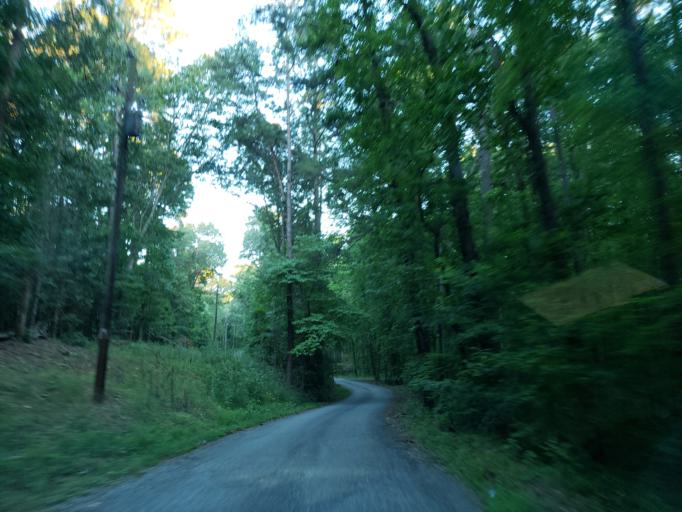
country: US
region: Georgia
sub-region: Bartow County
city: Euharlee
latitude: 34.0945
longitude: -84.8729
